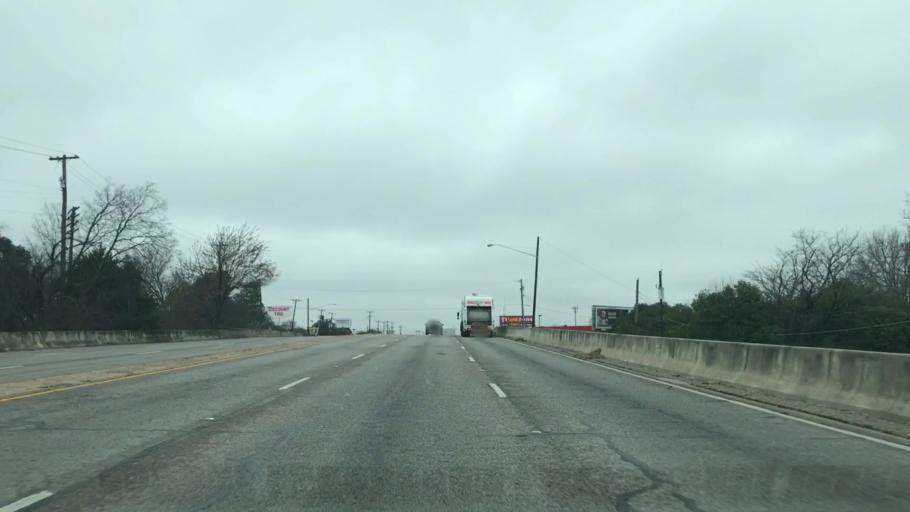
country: US
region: Texas
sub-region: Dallas County
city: Highland Park
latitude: 32.8556
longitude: -96.7434
